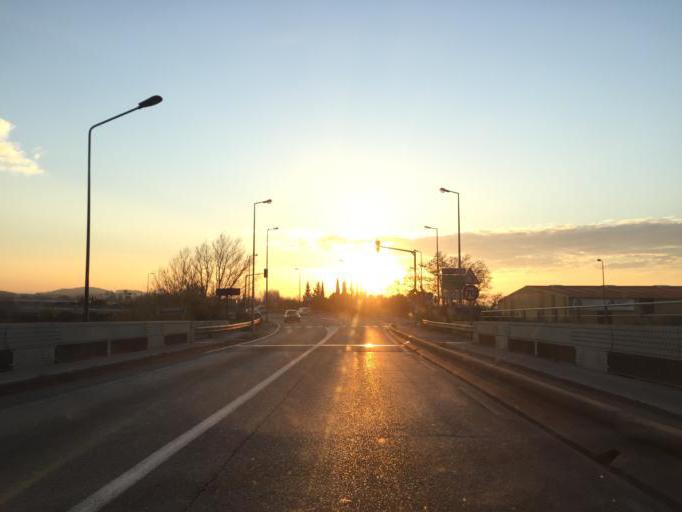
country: FR
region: Provence-Alpes-Cote d'Azur
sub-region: Departement du Vaucluse
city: Cavaillon
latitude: 43.8260
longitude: 5.0295
